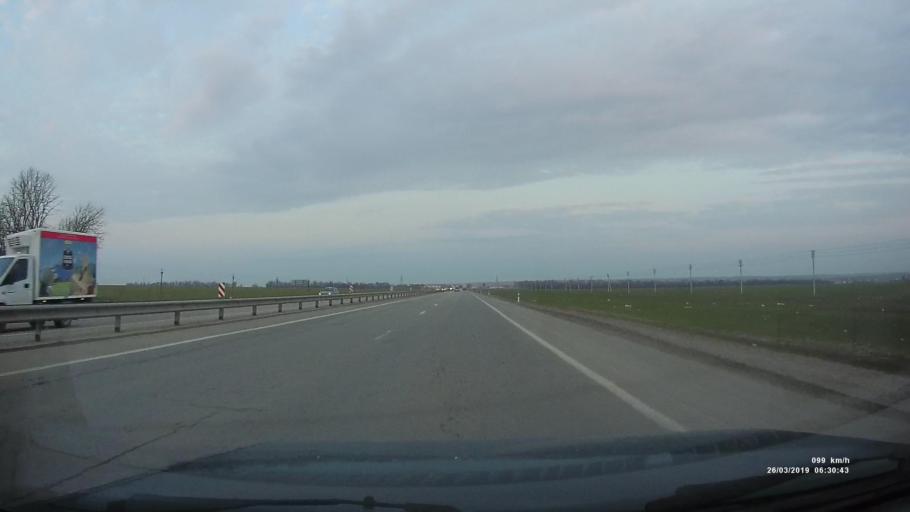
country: RU
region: Rostov
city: Krym
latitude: 47.2718
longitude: 39.5466
